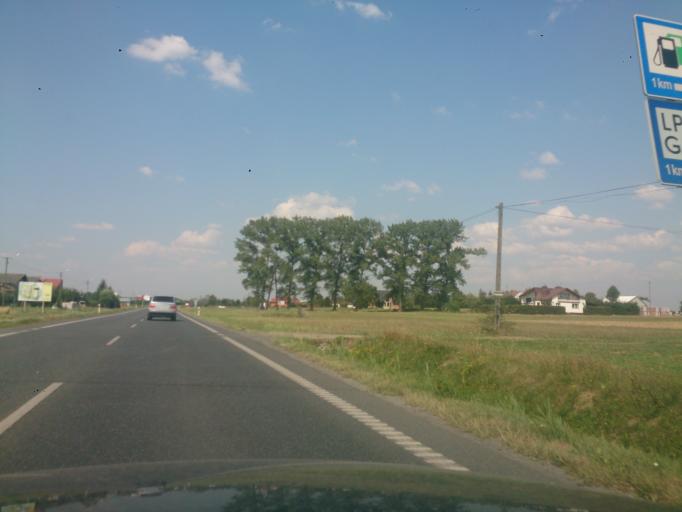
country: PL
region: Subcarpathian Voivodeship
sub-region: Powiat kolbuszowski
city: Kolbuszowa
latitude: 50.2616
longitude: 21.7613
